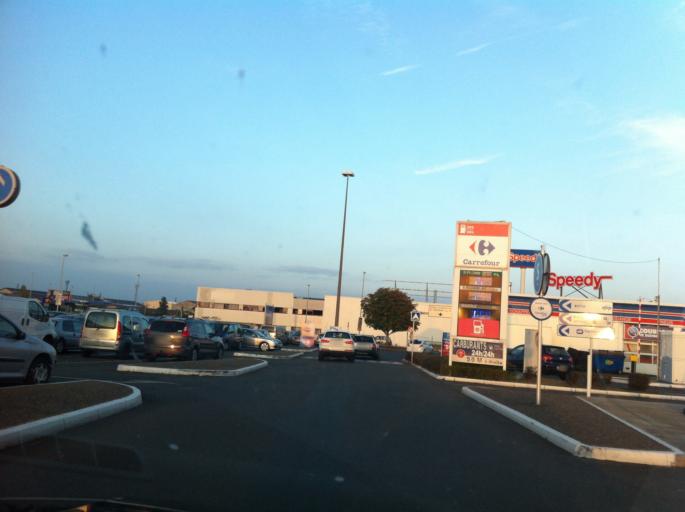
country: FR
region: Centre
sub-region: Departement d'Indre-et-Loire
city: Saint-Avertin
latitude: 47.3746
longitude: 0.7165
